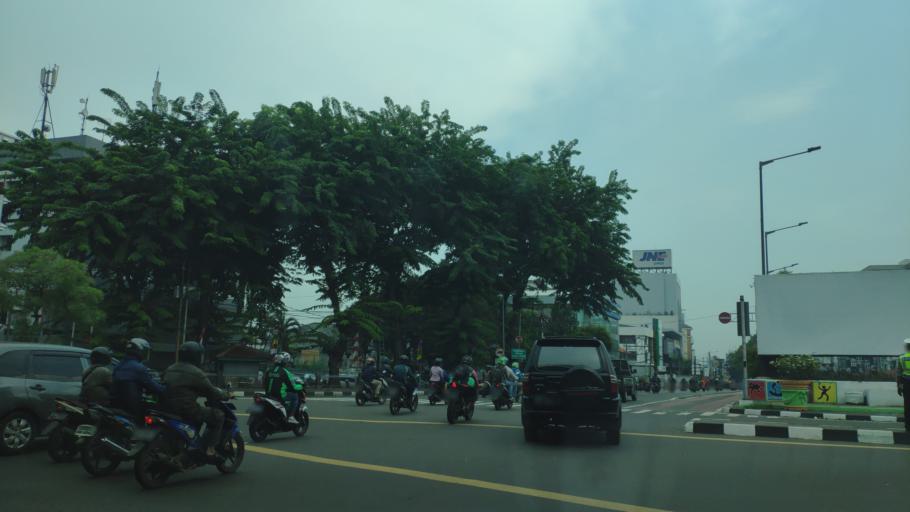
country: ID
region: Jakarta Raya
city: Jakarta
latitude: -6.1794
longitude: 106.7962
